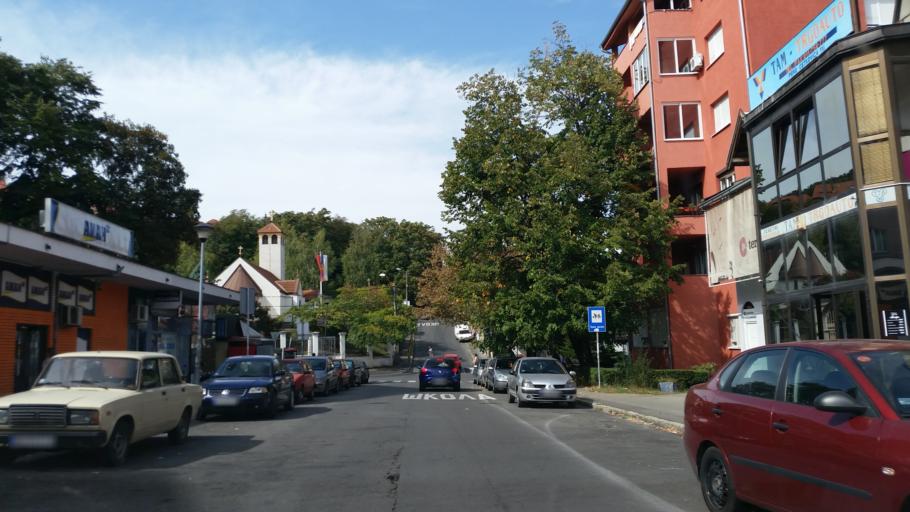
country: RS
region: Central Serbia
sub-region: Belgrade
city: Palilula
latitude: 44.8096
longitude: 20.5163
